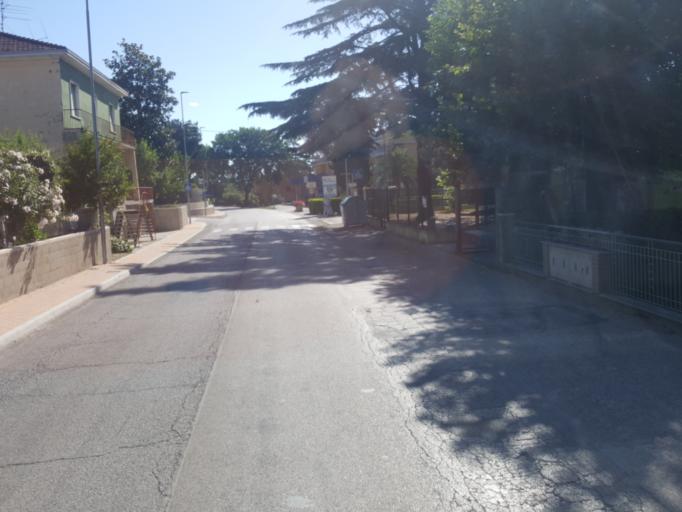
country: IT
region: The Marches
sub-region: Provincia di Pesaro e Urbino
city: Rio Salso-Case Bernardi
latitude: 43.8358
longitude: 12.6908
